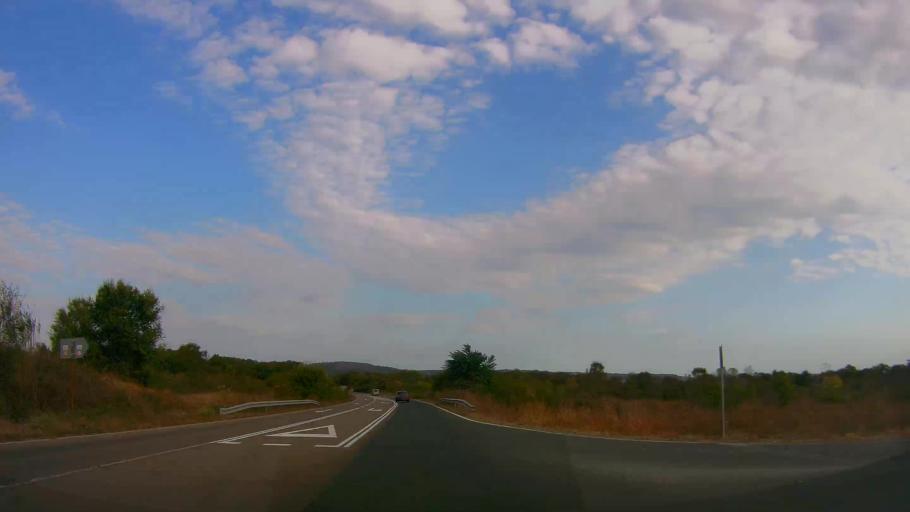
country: BG
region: Burgas
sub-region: Obshtina Sozopol
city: Sozopol
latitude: 42.3457
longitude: 27.7148
